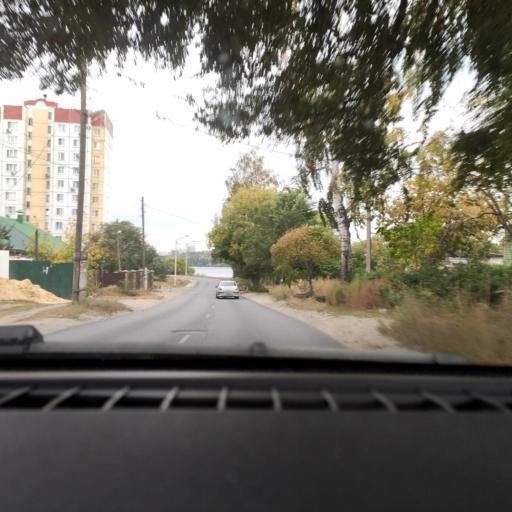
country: RU
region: Voronezj
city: Voronezh
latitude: 51.6979
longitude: 39.2590
